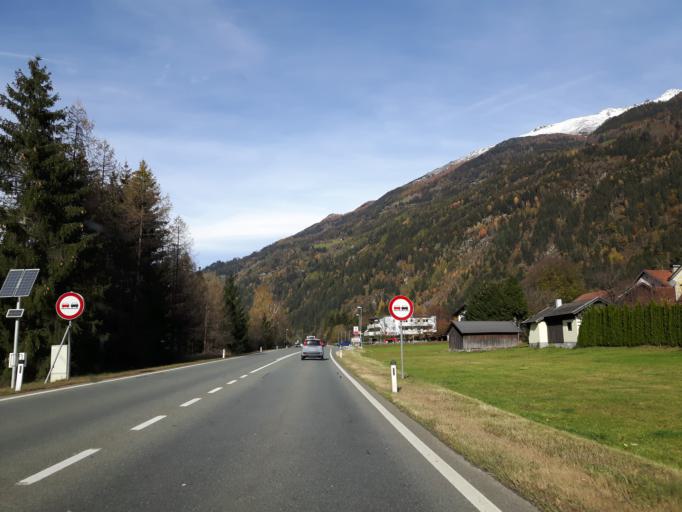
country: AT
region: Tyrol
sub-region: Politischer Bezirk Lienz
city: Ainet
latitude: 46.8638
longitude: 12.6883
